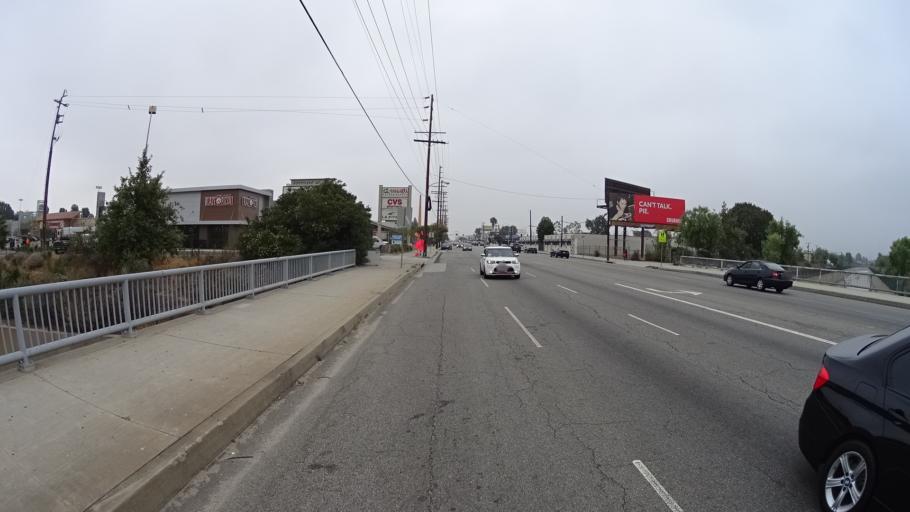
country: US
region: California
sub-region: Los Angeles County
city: Van Nuys
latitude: 34.1867
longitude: -118.4177
